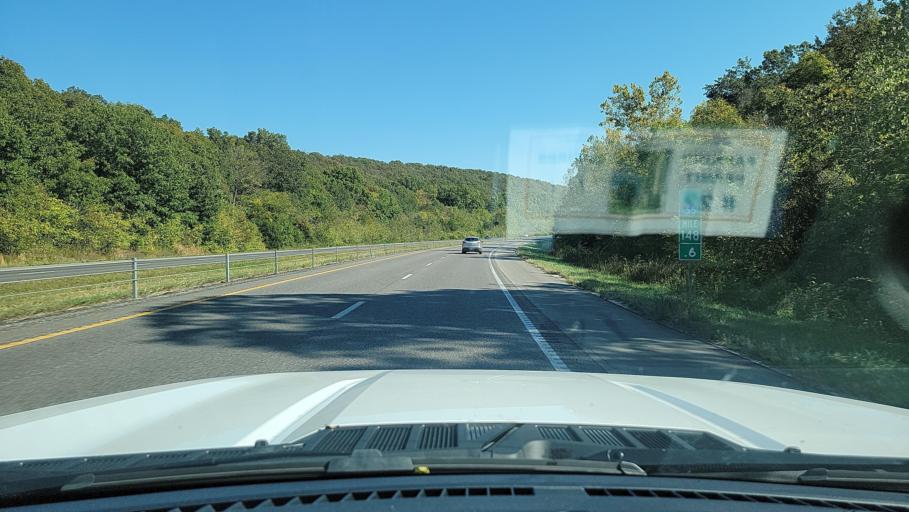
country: US
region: Missouri
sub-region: Sainte Genevieve County
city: Sainte Genevieve
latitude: 37.9240
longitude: -90.0960
